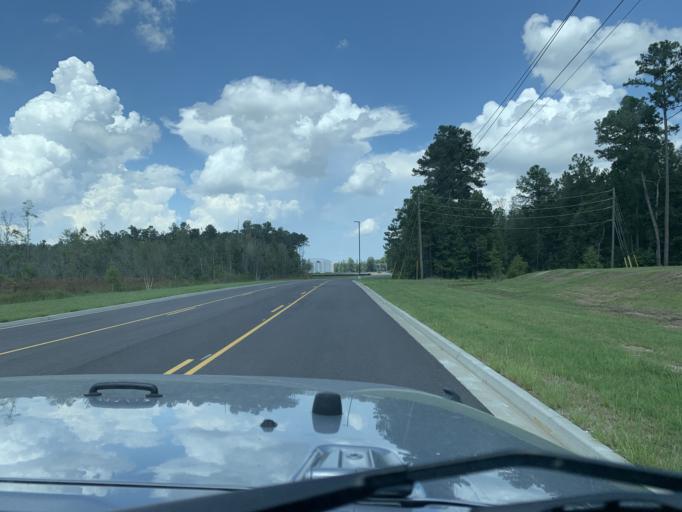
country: US
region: Georgia
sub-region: Chatham County
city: Bloomingdale
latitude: 32.1104
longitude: -81.2784
